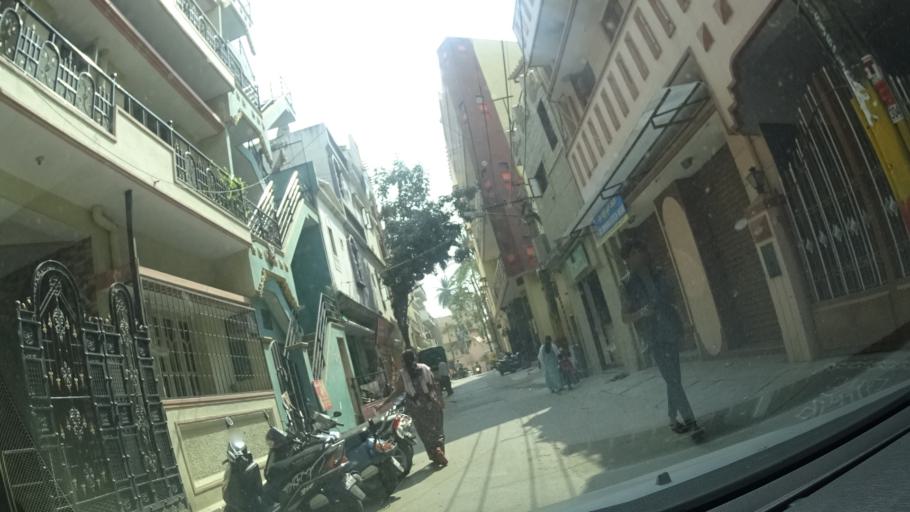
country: IN
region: Karnataka
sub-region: Bangalore Urban
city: Bangalore
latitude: 12.9584
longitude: 77.5575
